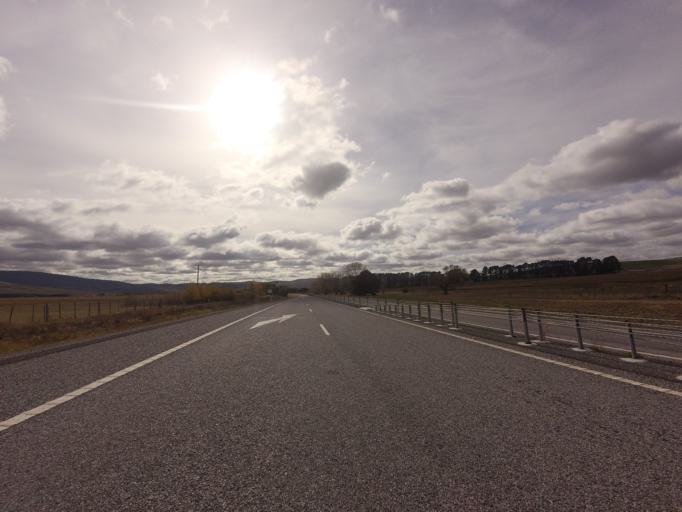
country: AU
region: Tasmania
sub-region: Brighton
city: Bridgewater
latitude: -42.4961
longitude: 147.1858
